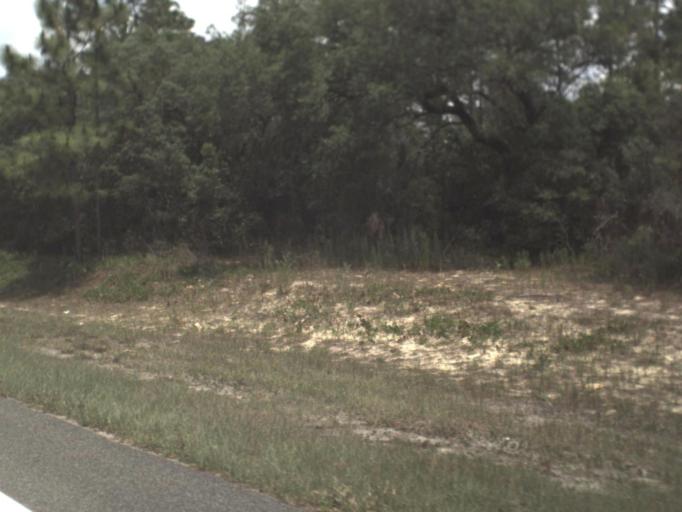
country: US
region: Florida
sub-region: Putnam County
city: Crescent City
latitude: 29.4087
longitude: -81.7369
